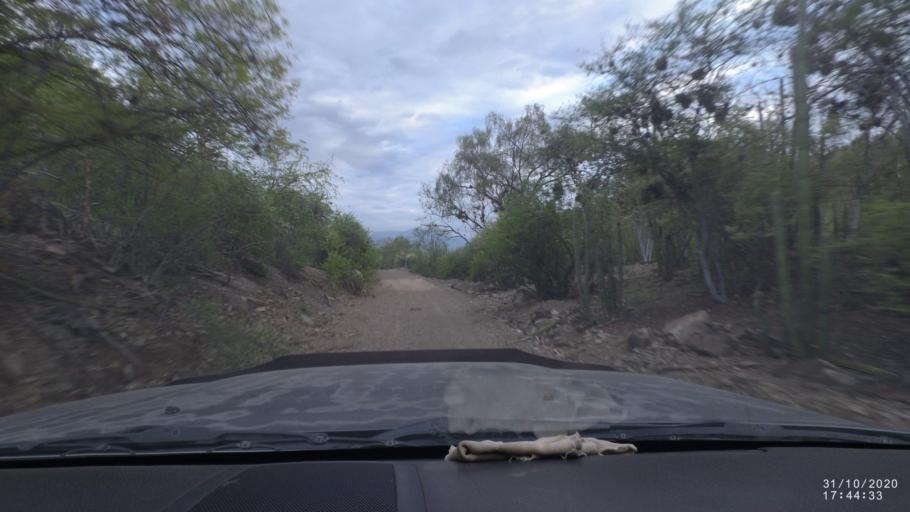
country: BO
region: Chuquisaca
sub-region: Provincia Zudanez
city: Mojocoya
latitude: -18.6111
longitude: -64.5469
